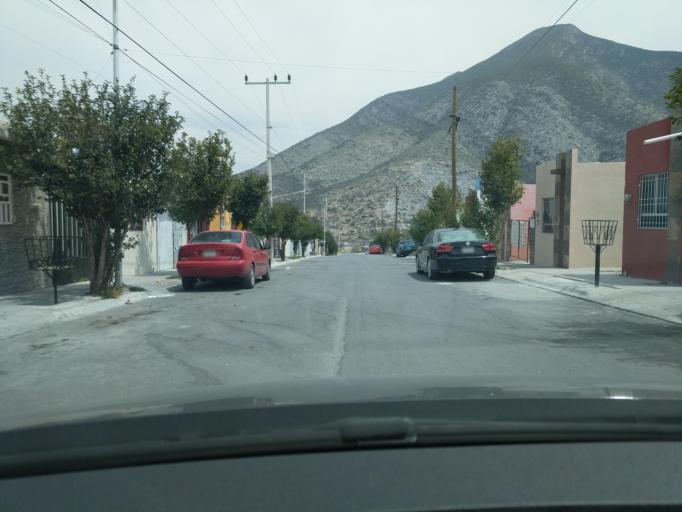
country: MX
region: Coahuila
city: Saltillo
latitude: 25.3447
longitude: -101.0064
